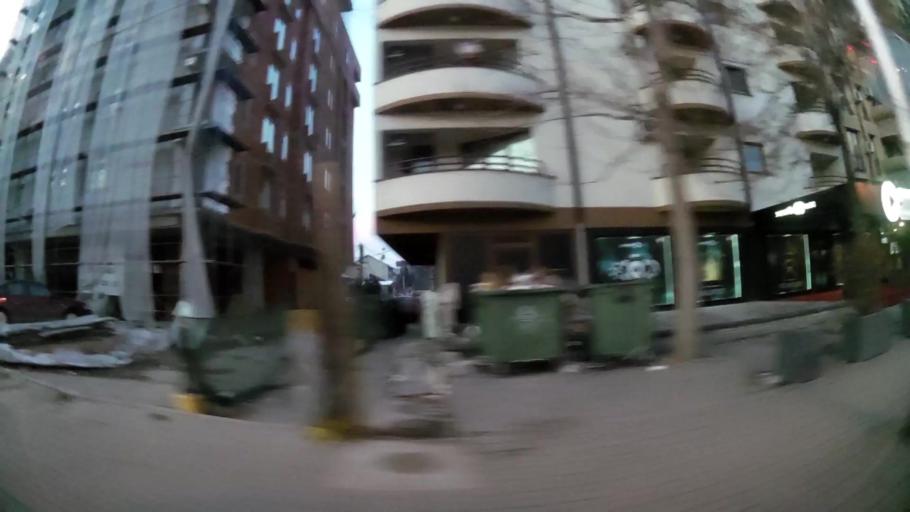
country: MK
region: Karpos
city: Skopje
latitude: 41.9956
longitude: 21.4109
